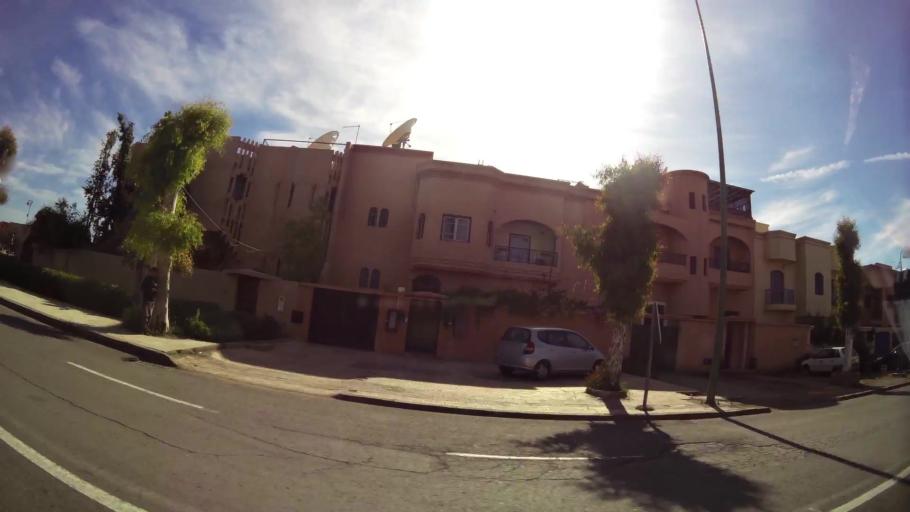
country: MA
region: Marrakech-Tensift-Al Haouz
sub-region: Marrakech
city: Marrakesh
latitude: 31.6479
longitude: -8.0471
